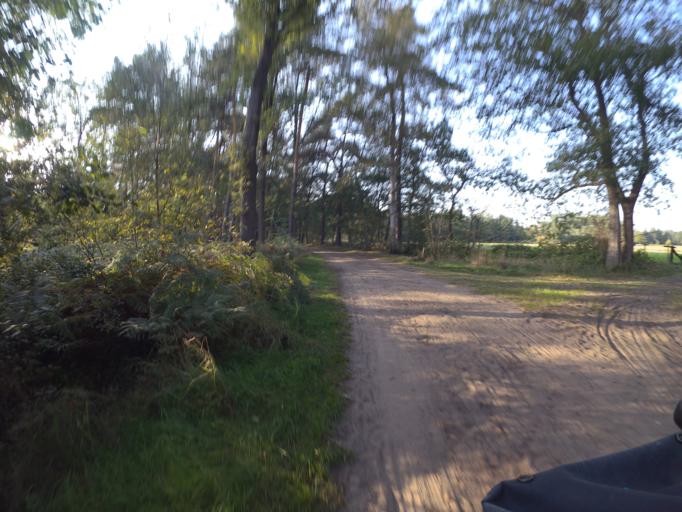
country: NL
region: North Brabant
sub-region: Gemeente Oirschot
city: Oirschot
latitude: 51.5372
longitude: 5.3254
